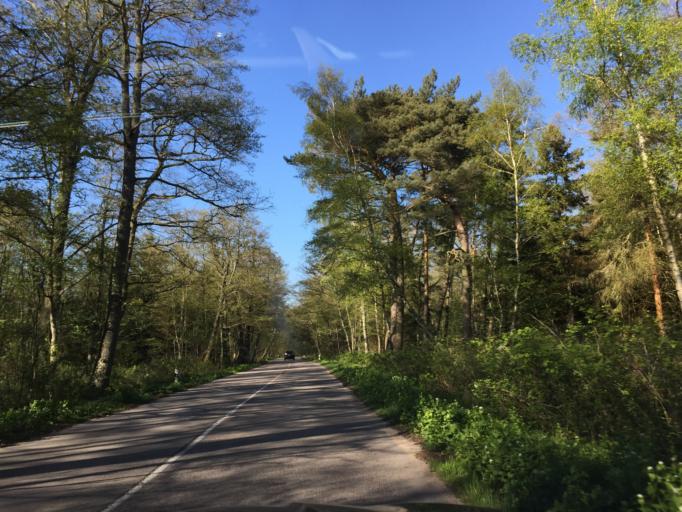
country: LT
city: Nida
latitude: 55.1932
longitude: 20.8620
